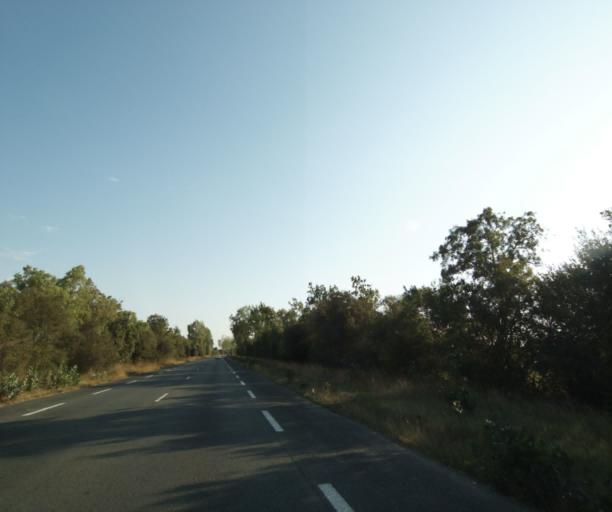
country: FR
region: Poitou-Charentes
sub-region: Departement de la Charente-Maritime
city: Saint-Hippolyte
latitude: 45.9239
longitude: -0.8819
